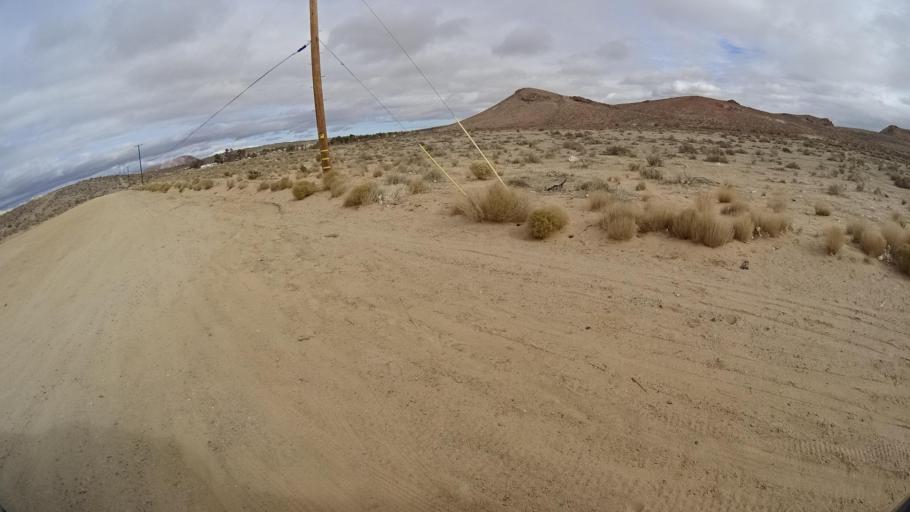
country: US
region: California
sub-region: Kern County
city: Rosamond
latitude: 34.8915
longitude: -118.2027
